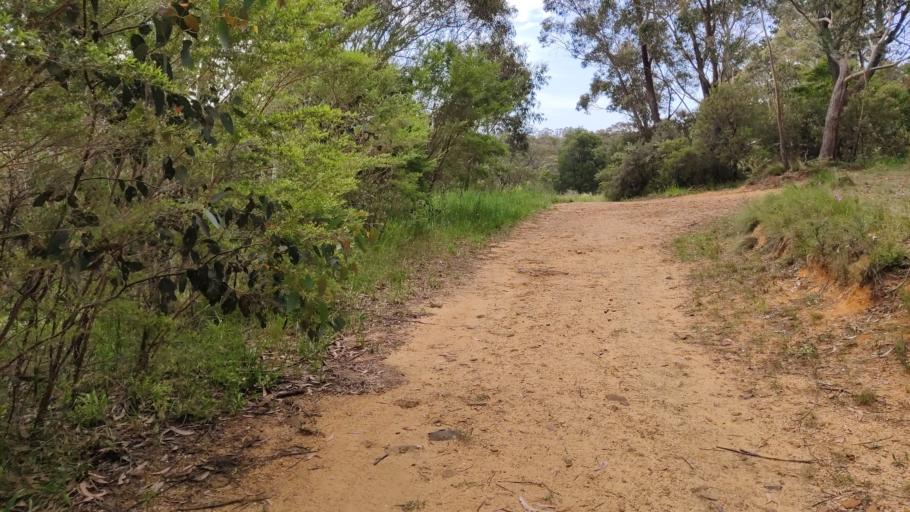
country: AU
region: New South Wales
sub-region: Blue Mountains Municipality
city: Leura
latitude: -33.7190
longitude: 150.3265
